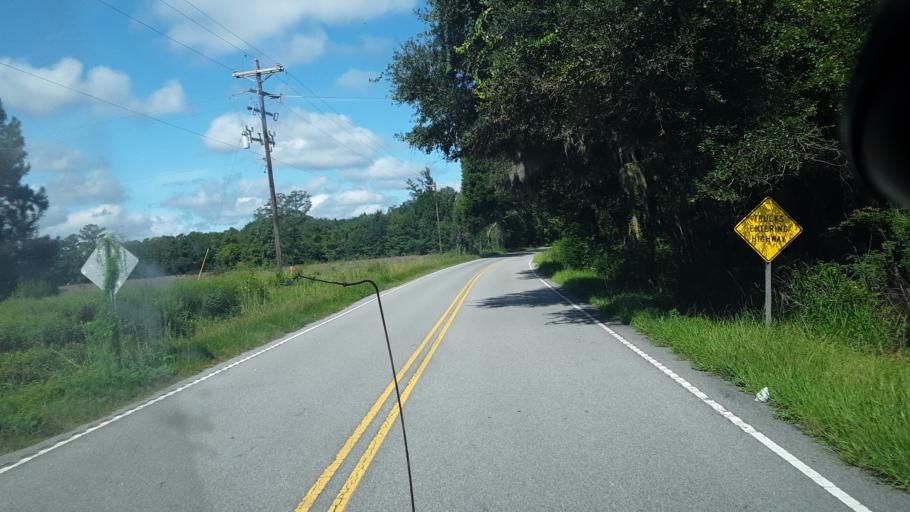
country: US
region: South Carolina
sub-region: Jasper County
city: Ridgeland
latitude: 32.5917
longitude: -80.9773
